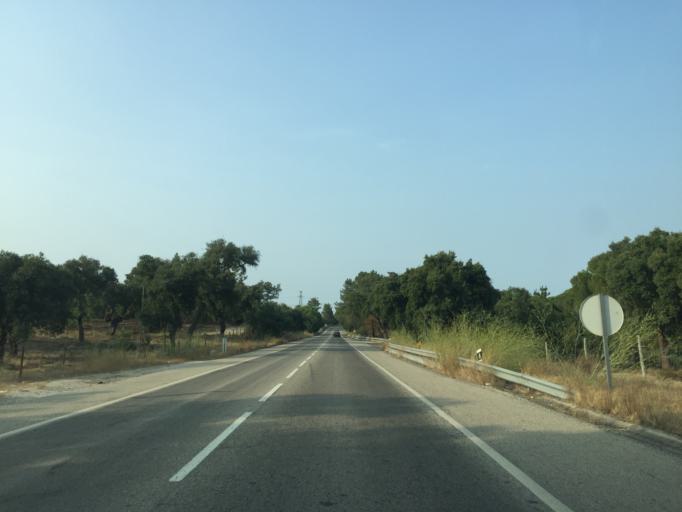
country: PT
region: Setubal
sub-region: Setubal
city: Setubal
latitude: 38.5862
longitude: -8.6785
